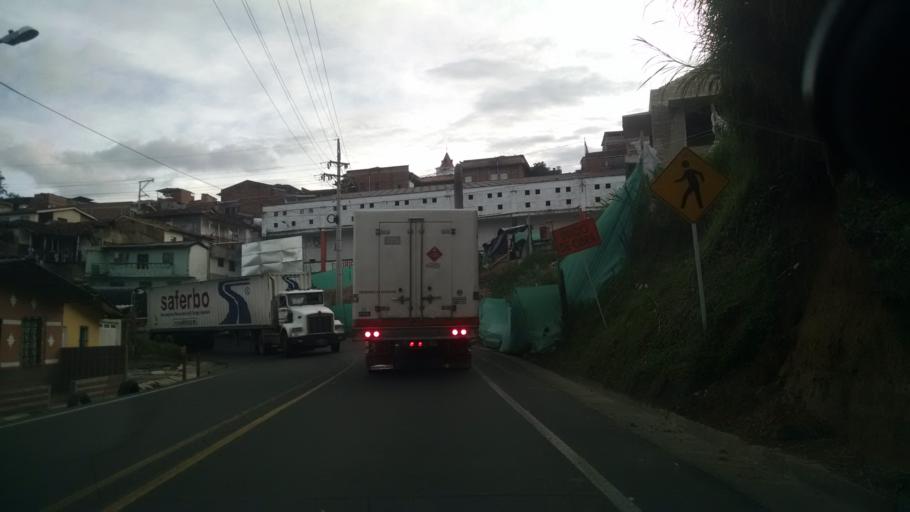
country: CO
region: Antioquia
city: Santa Barbara
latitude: 5.8758
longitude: -75.5661
